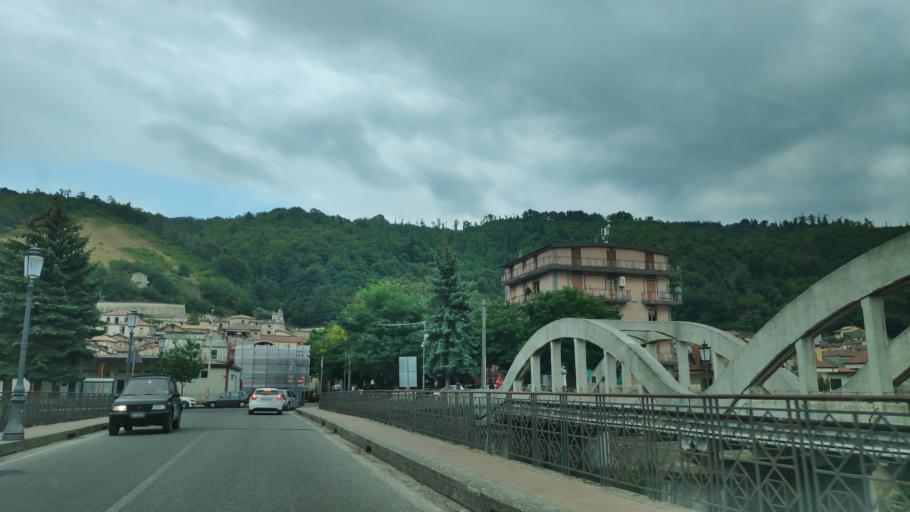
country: IT
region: Calabria
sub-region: Provincia di Catanzaro
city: Cardinale
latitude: 38.6441
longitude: 16.3863
